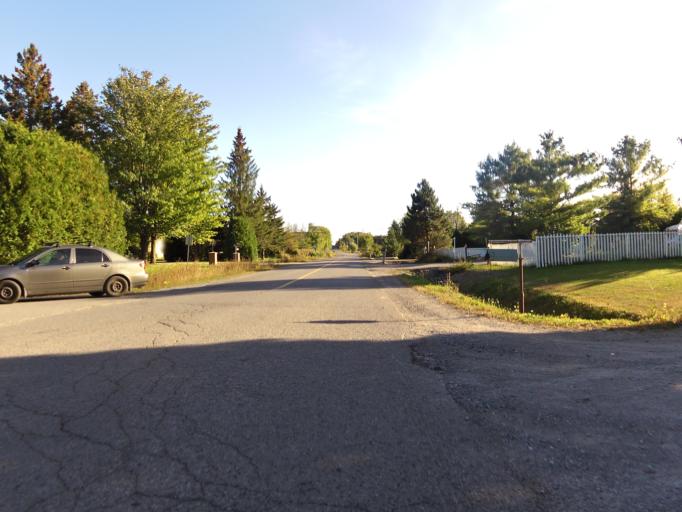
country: CA
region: Ontario
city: Bells Corners
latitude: 45.4543
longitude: -75.8835
